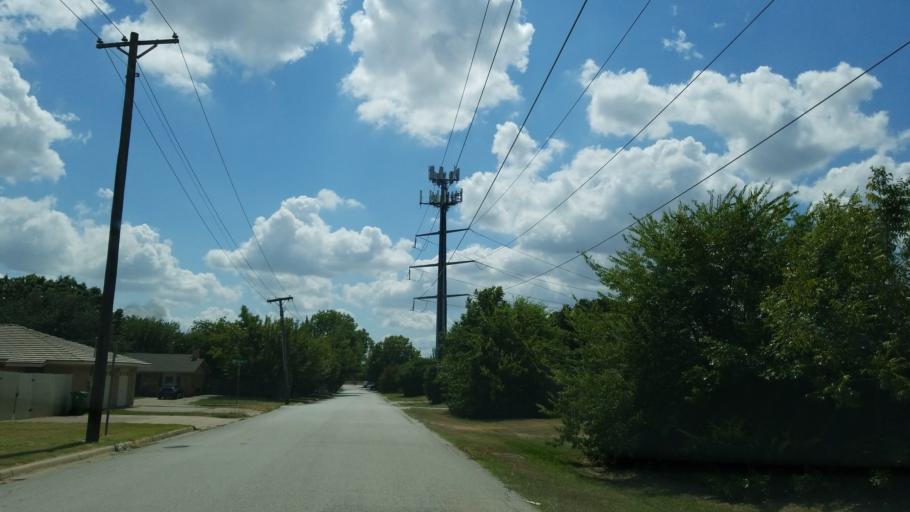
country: US
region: Texas
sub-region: Tarrant County
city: Grapevine
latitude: 32.9273
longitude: -97.0843
